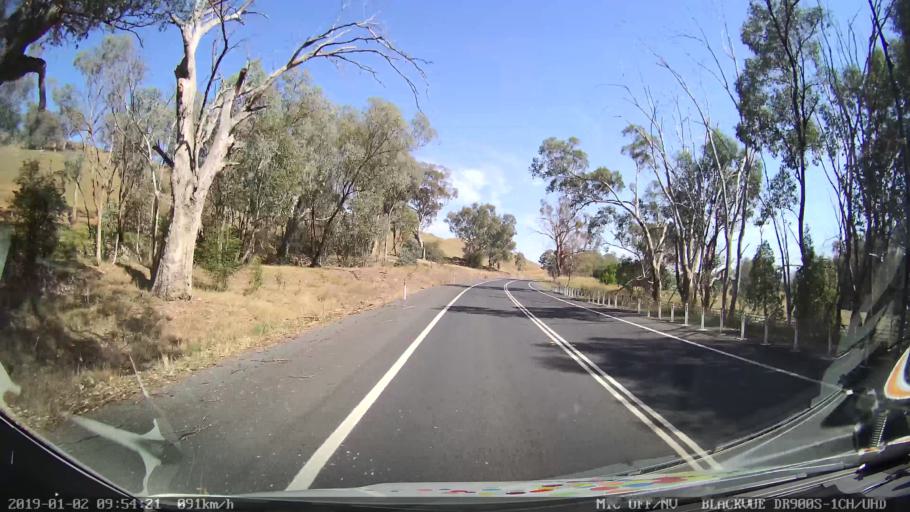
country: AU
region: New South Wales
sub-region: Tumut Shire
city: Tumut
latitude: -35.2364
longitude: 148.1967
